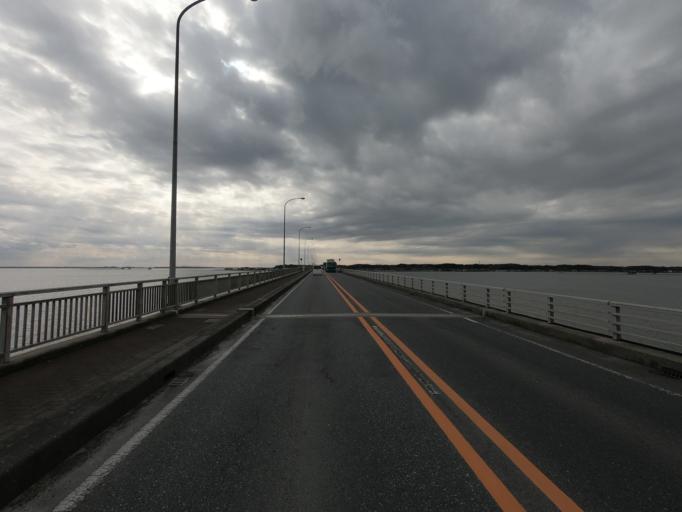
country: JP
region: Ibaraki
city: Inashiki
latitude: 36.0943
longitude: 140.4014
